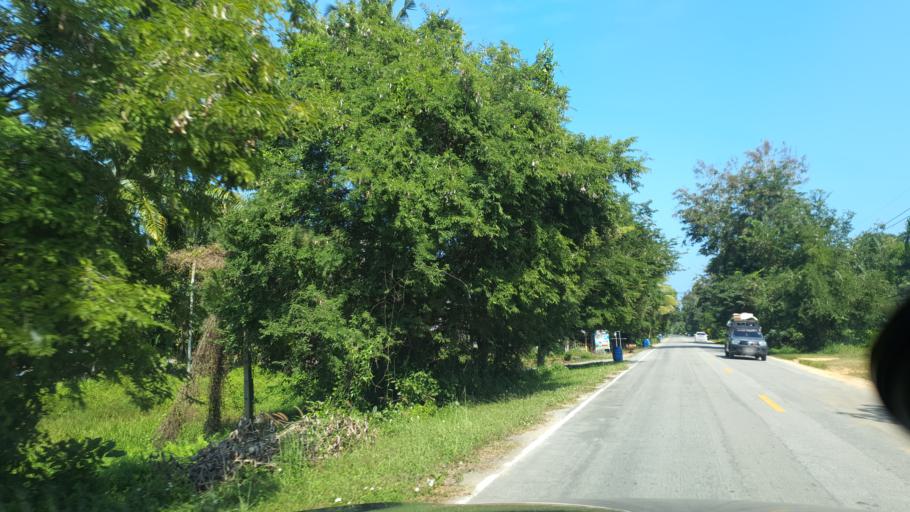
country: TH
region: Surat Thani
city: Tha Chana
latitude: 9.5820
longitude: 99.1946
